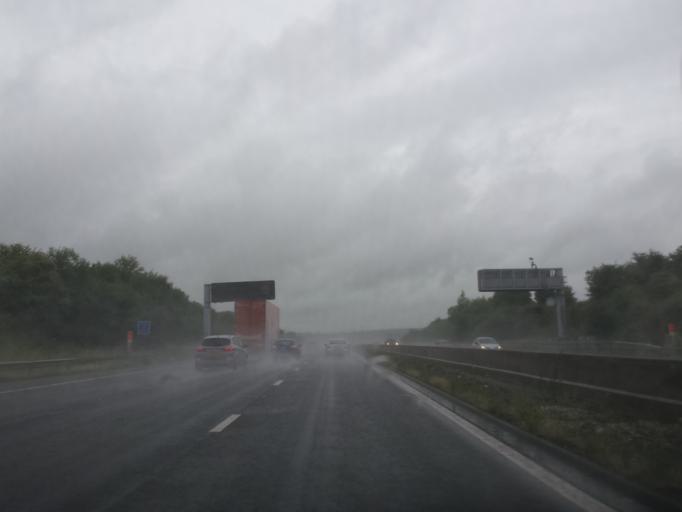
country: GB
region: England
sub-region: Doncaster
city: Conisbrough
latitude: 53.4531
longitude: -1.2179
